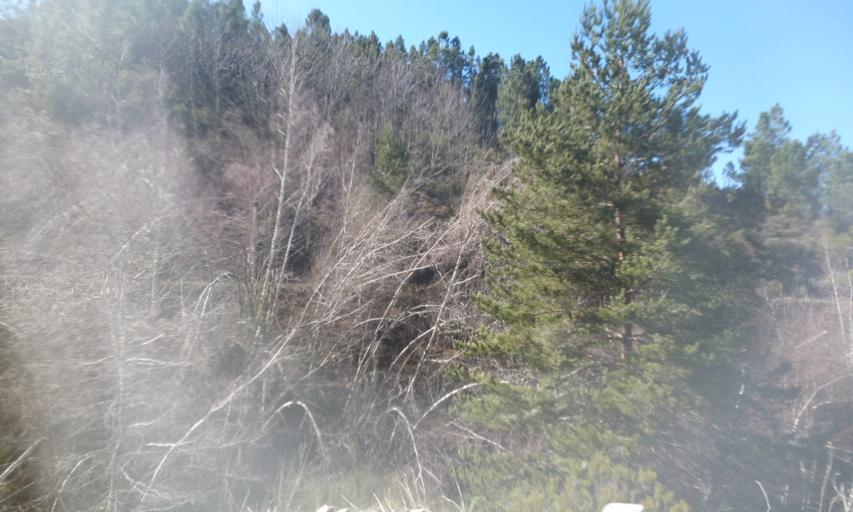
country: PT
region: Guarda
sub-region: Manteigas
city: Manteigas
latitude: 40.4414
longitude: -7.5050
